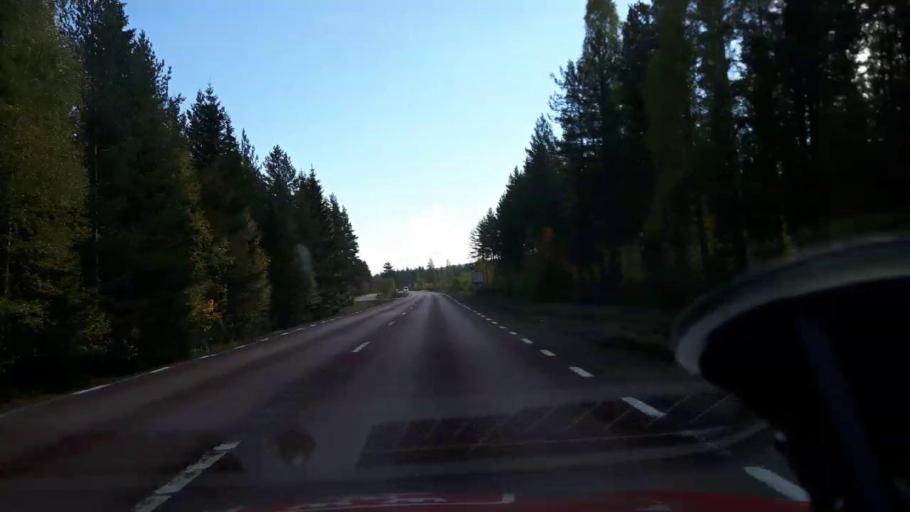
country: SE
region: Gaevleborg
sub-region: Ljusdals Kommun
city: Farila
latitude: 61.9327
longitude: 15.5330
